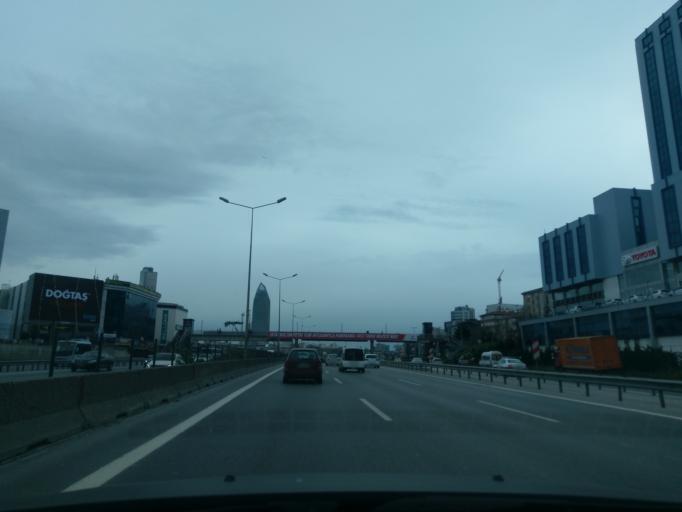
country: TR
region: Istanbul
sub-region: Atasehir
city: Atasehir
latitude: 40.9873
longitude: 29.0867
